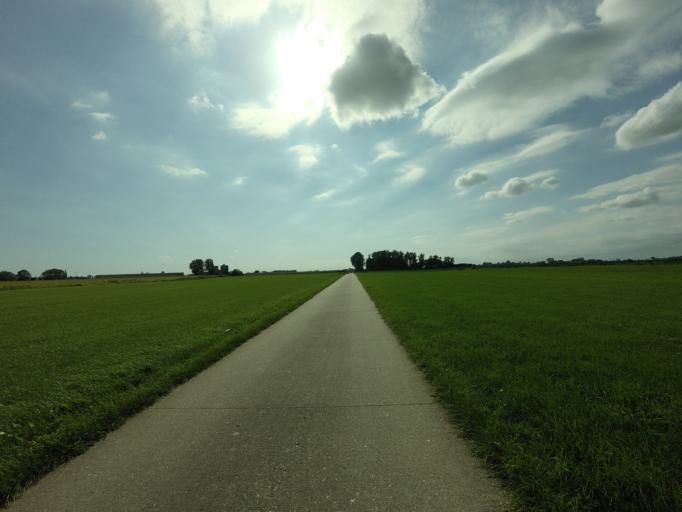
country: NL
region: Friesland
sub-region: Gemeente Littenseradiel
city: Makkum
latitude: 53.0876
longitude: 5.6339
